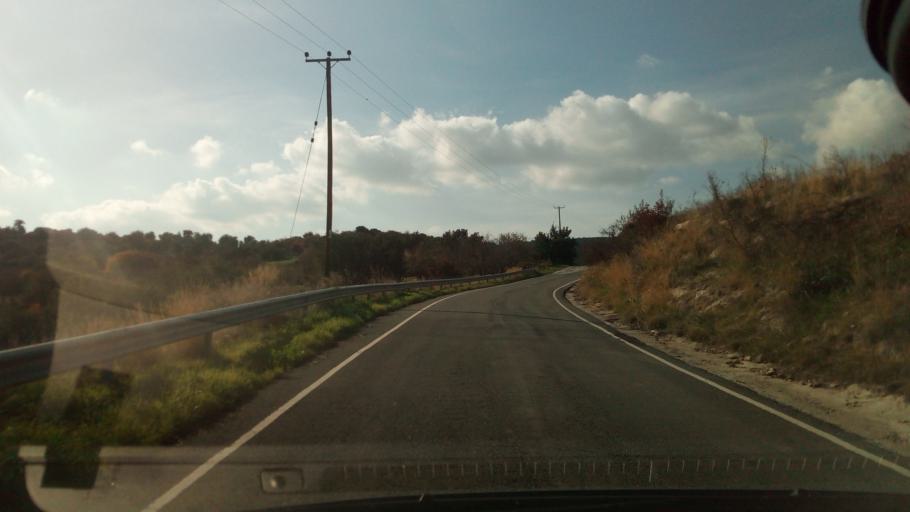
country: CY
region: Pafos
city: Polis
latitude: 34.9696
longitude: 32.4502
